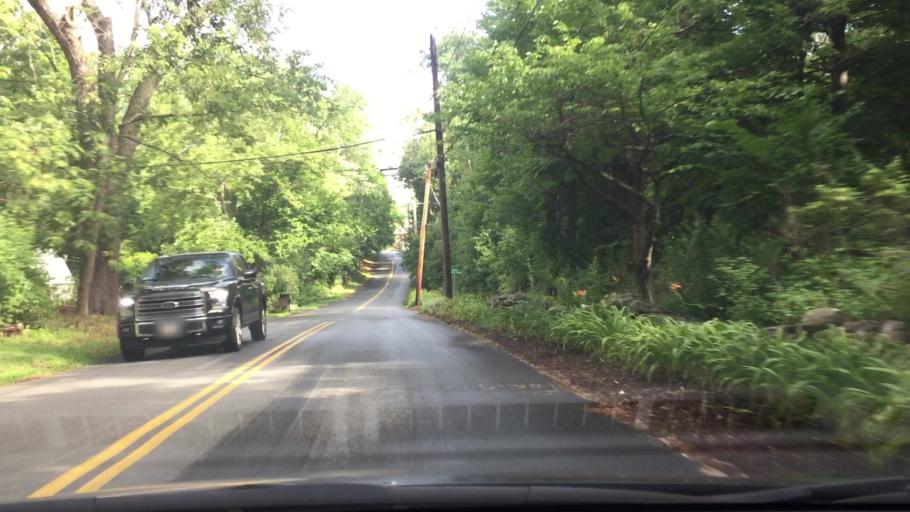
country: US
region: Massachusetts
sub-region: Middlesex County
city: Acton
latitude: 42.4973
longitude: -71.4372
